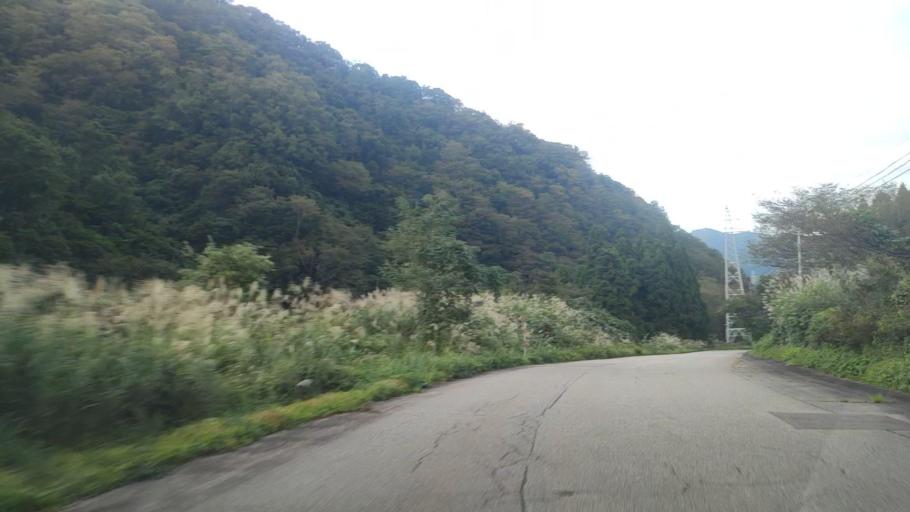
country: JP
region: Toyama
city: Yatsuomachi-higashikumisaka
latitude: 36.4609
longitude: 137.0838
